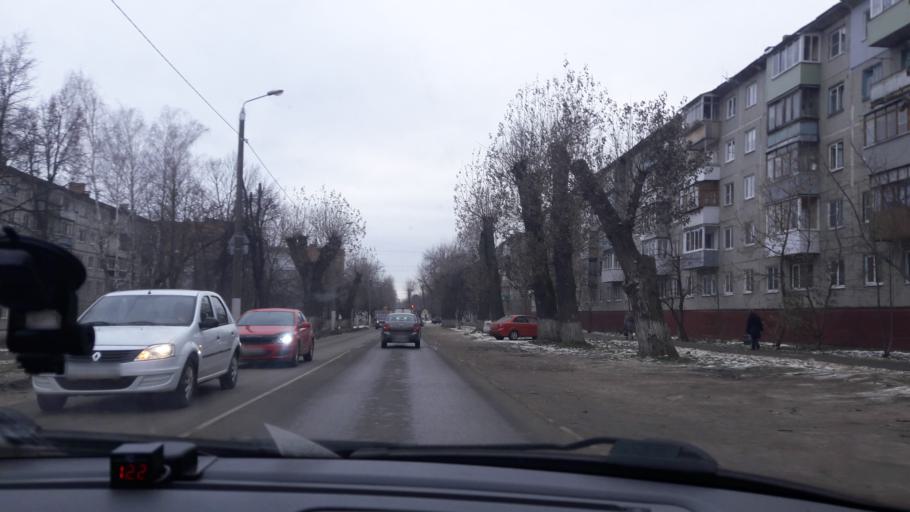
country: RU
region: Tula
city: Tula
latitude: 54.2008
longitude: 37.6564
